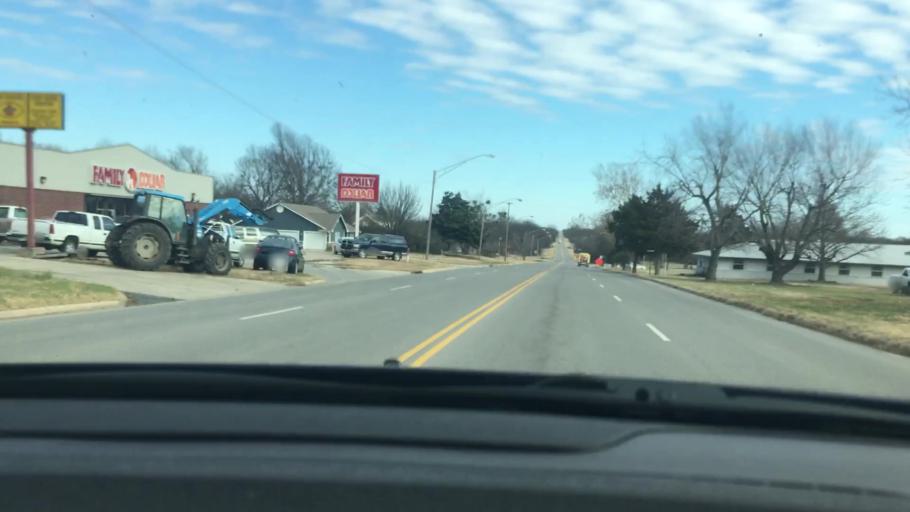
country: US
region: Oklahoma
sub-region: Garvin County
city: Stratford
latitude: 34.7966
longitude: -96.9522
